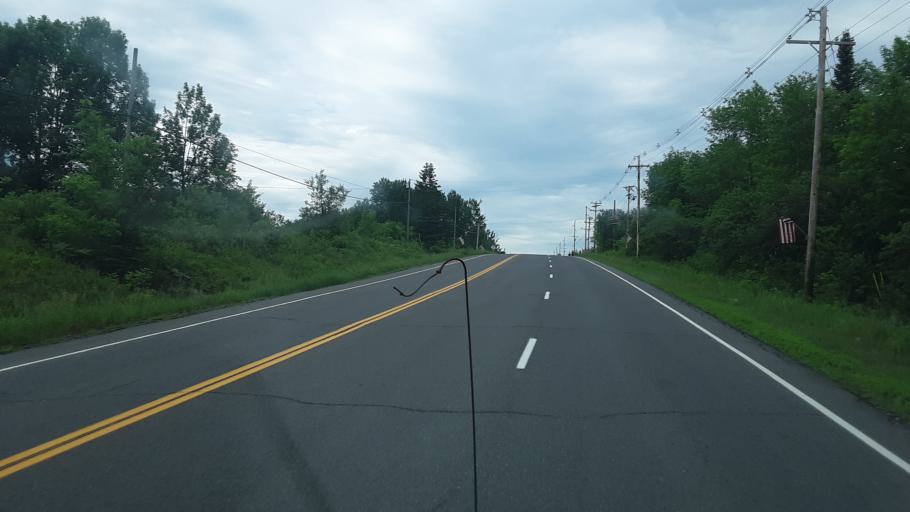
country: US
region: Maine
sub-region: Penobscot County
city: Patten
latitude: 45.9893
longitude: -68.4494
